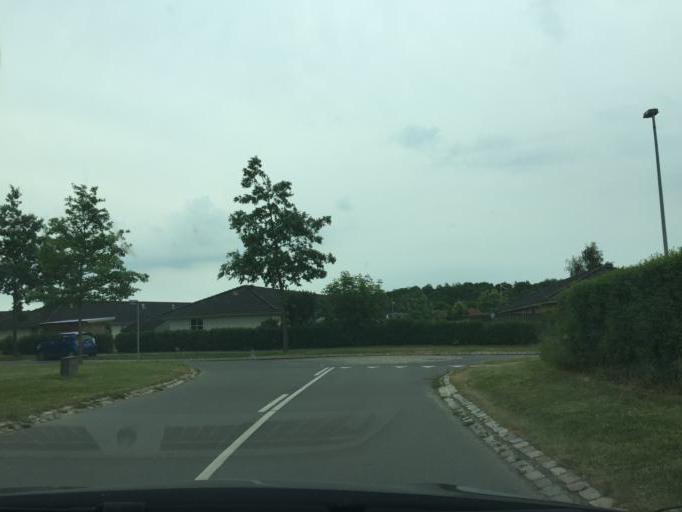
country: DK
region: South Denmark
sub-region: Odense Kommune
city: Neder Holluf
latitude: 55.3637
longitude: 10.4707
